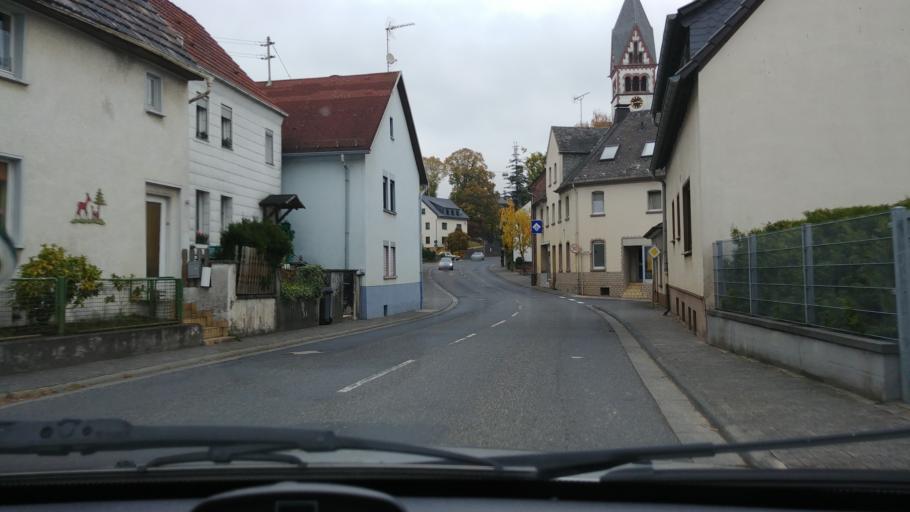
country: DE
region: Rheinland-Pfalz
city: Irmtraut
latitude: 50.5383
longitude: 8.0437
